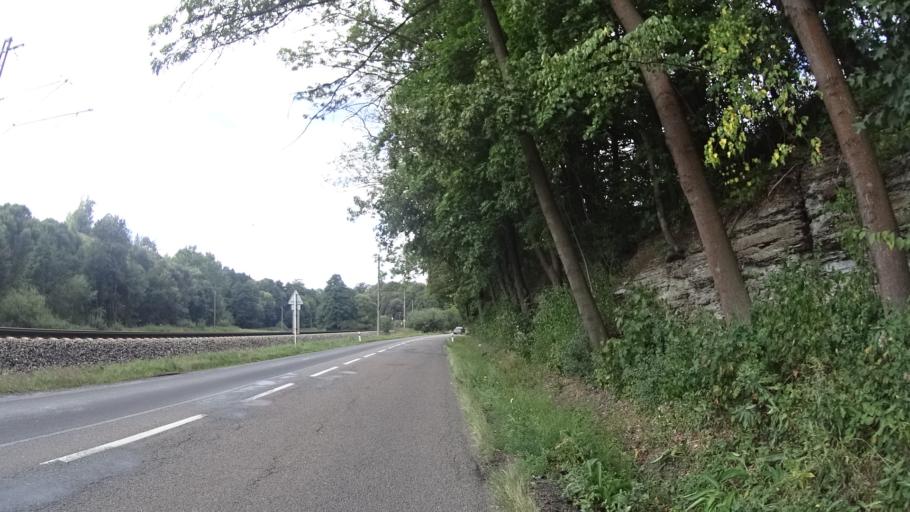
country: CZ
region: Pardubicky
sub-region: Okres Usti nad Orlici
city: Usti nad Orlici
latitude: 49.9871
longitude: 16.4232
